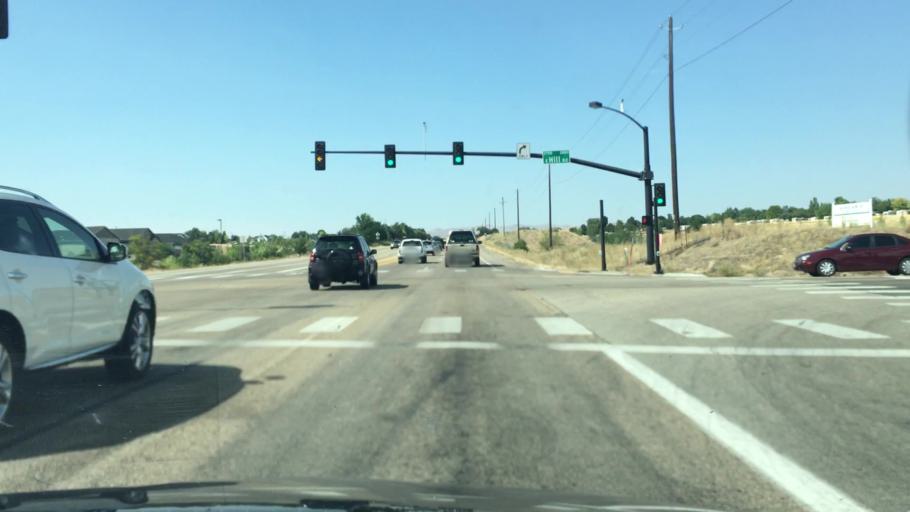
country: US
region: Idaho
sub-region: Ada County
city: Eagle
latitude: 43.6933
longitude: -116.3191
